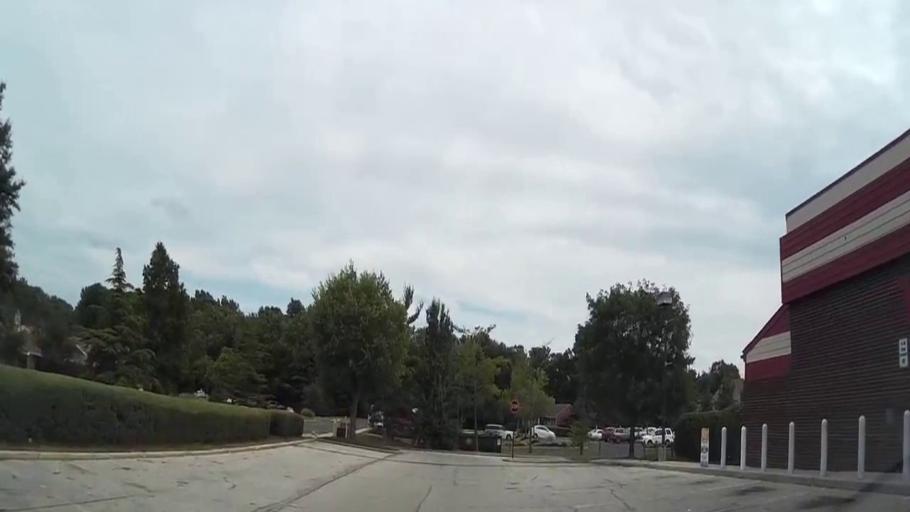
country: US
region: New Jersey
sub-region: Burlington County
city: Marlton
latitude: 39.8718
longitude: -74.9330
